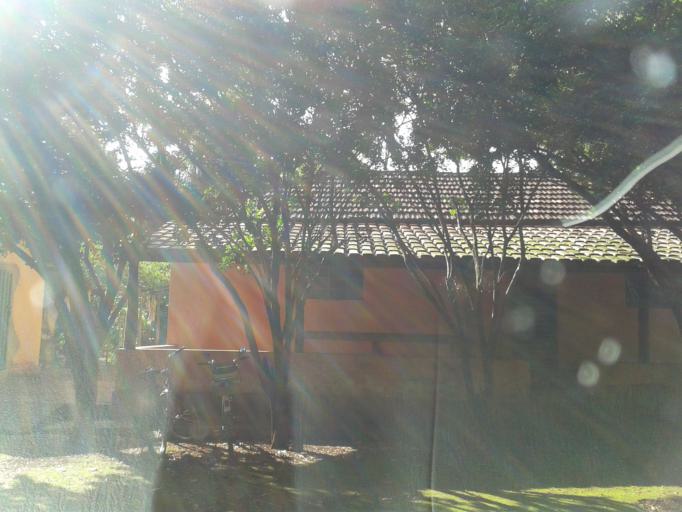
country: BR
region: Minas Gerais
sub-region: Centralina
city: Centralina
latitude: -18.7103
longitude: -49.1877
